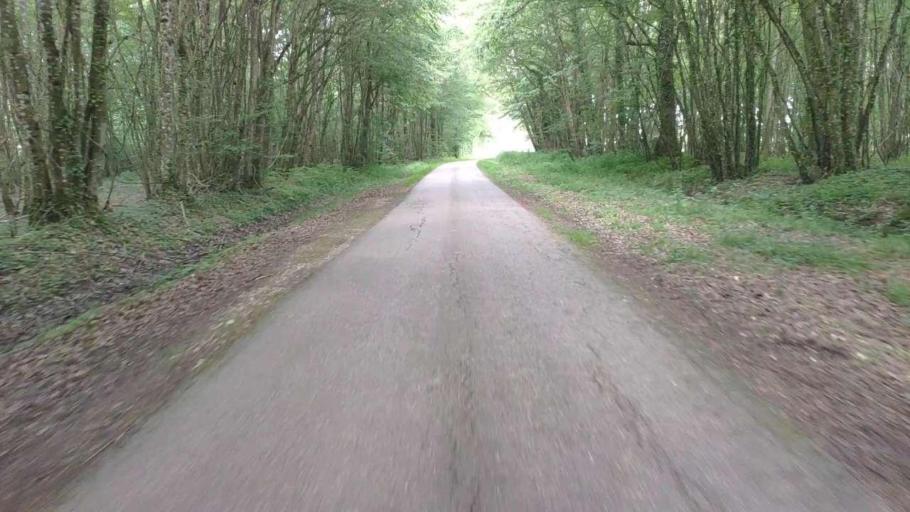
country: FR
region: Franche-Comte
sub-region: Departement du Jura
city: Bletterans
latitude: 46.7955
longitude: 5.3537
